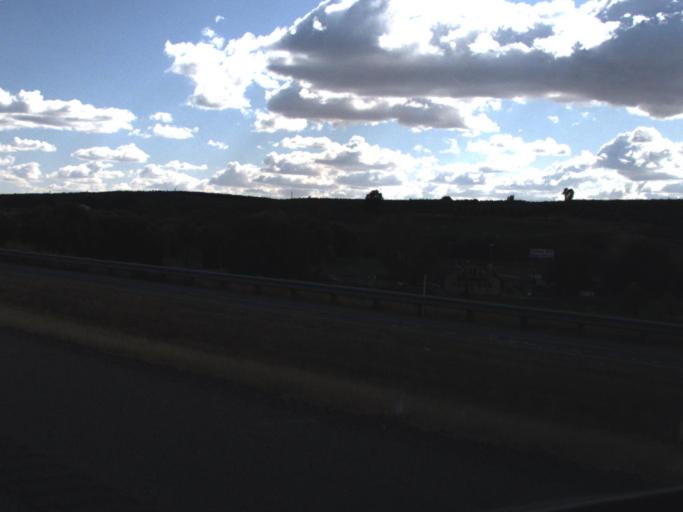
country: US
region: Washington
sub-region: Yakima County
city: Granger
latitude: 46.3438
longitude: -120.1752
